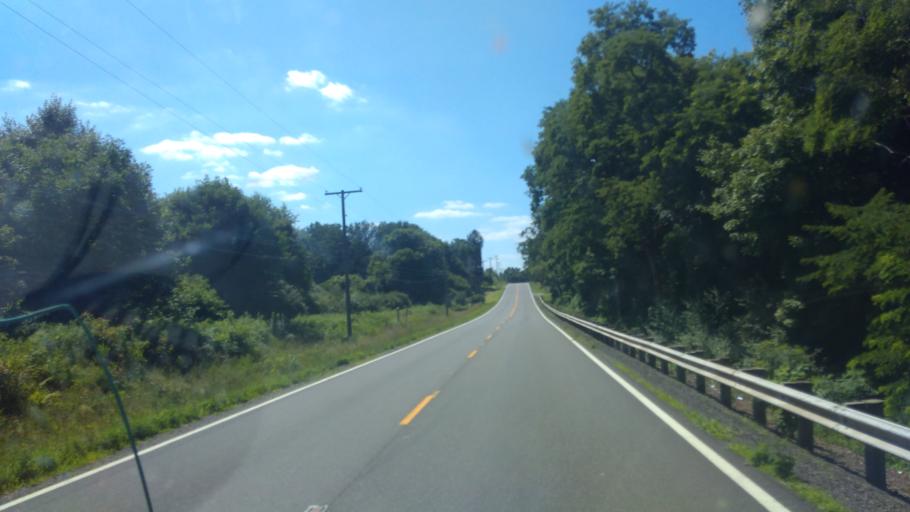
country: US
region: Ohio
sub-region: Carroll County
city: Carrollton
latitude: 40.5181
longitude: -81.0203
